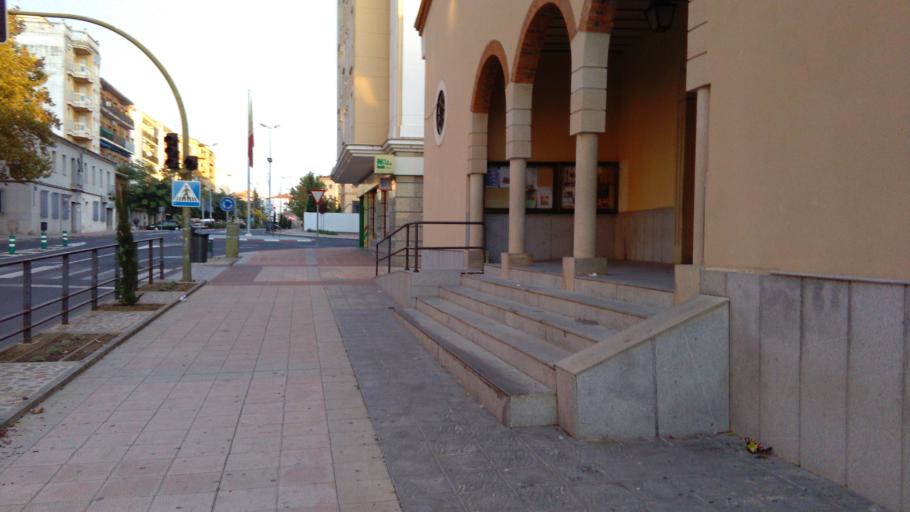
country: ES
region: Extremadura
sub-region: Provincia de Caceres
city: Coria
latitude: 39.9875
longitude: -6.5380
